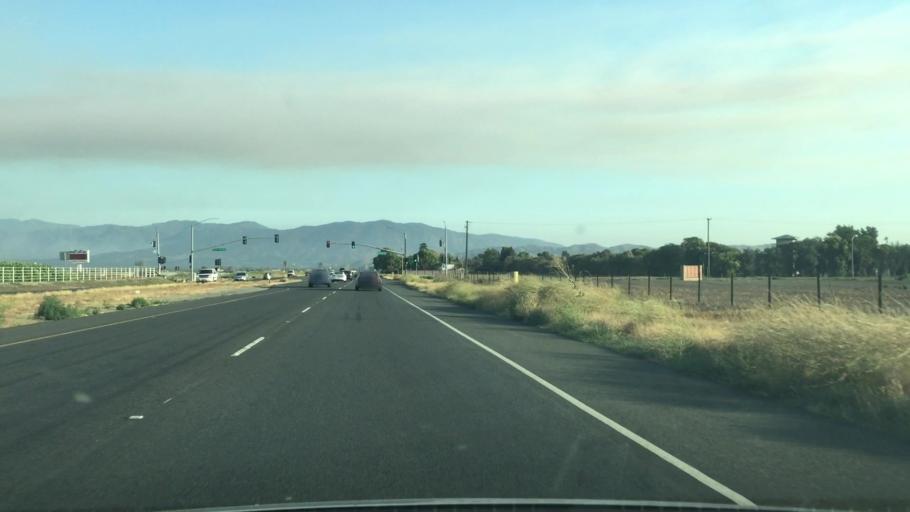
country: US
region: California
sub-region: San Bernardino County
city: Chino
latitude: 33.9844
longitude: -117.6509
